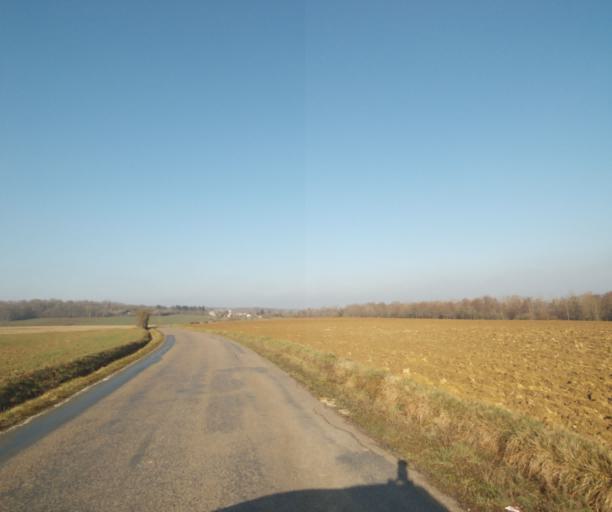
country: FR
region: Champagne-Ardenne
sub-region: Departement de la Haute-Marne
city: Wassy
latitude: 48.5028
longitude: 4.9272
